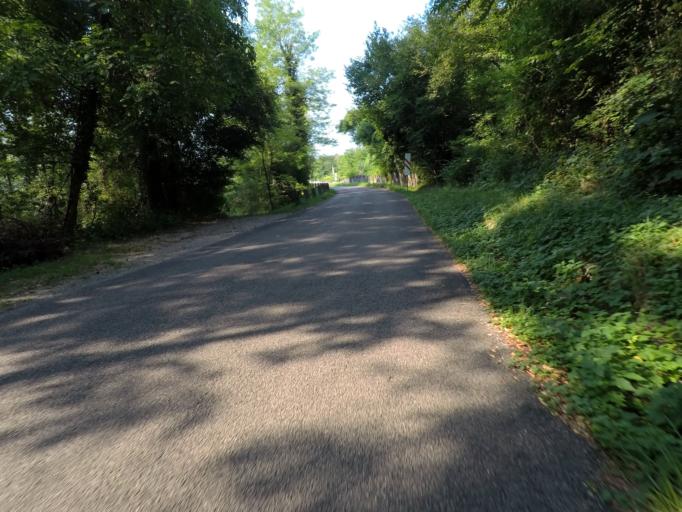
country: IT
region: Friuli Venezia Giulia
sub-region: Provincia di Pordenone
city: Pinzano al Tagliamento
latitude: 46.1925
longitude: 12.9540
